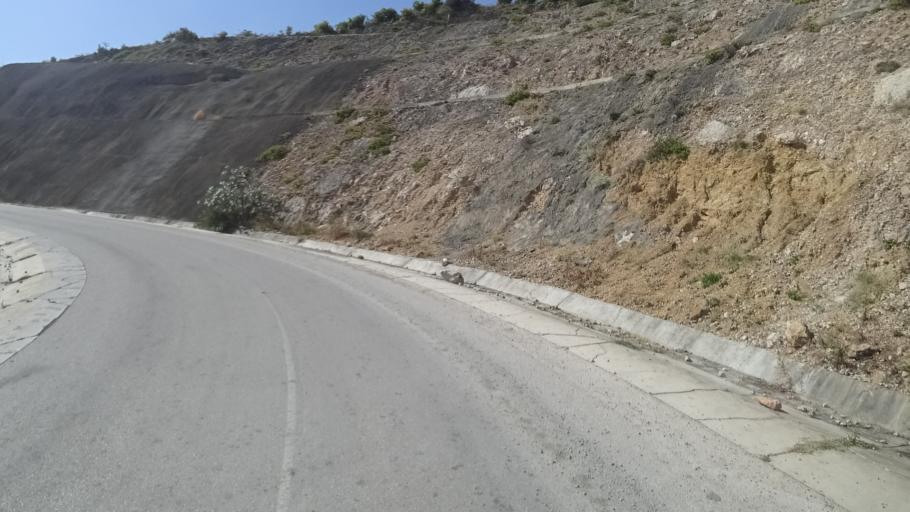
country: OM
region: Zufar
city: Salalah
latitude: 17.0485
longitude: 54.6130
